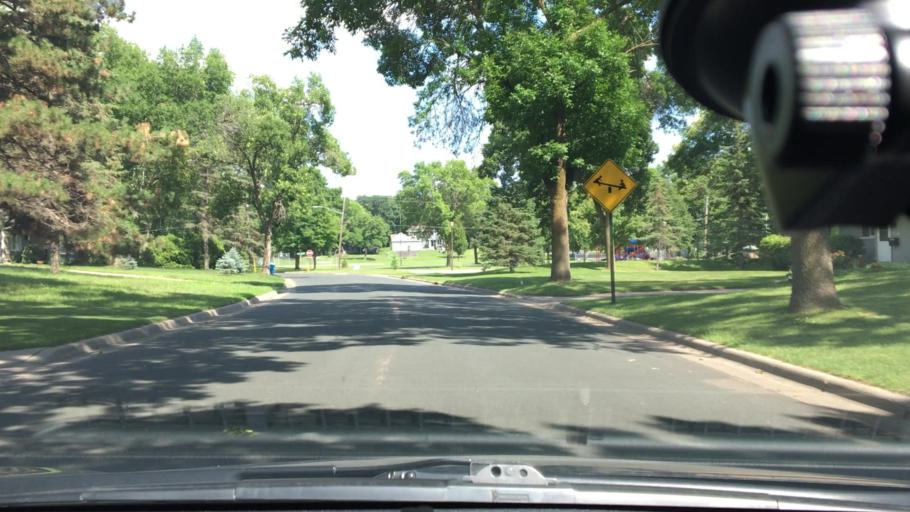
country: US
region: Minnesota
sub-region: Hennepin County
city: Golden Valley
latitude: 44.9972
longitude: -93.3867
